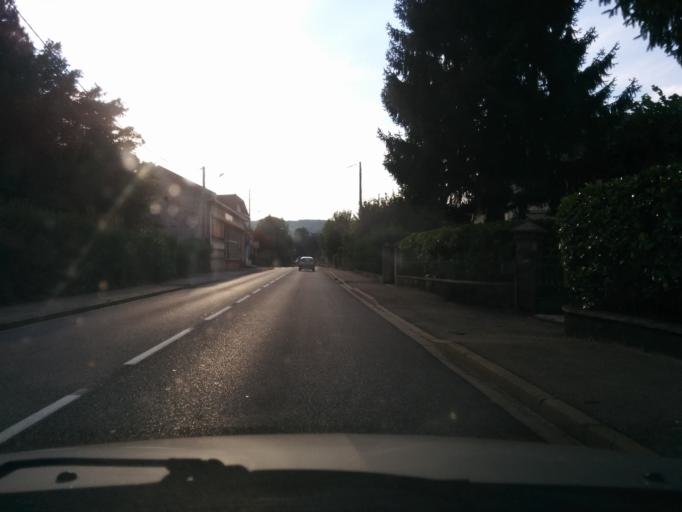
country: FR
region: Rhone-Alpes
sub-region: Departement de l'Isere
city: Saint-Laurent-du-Pont
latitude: 45.3879
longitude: 5.7294
